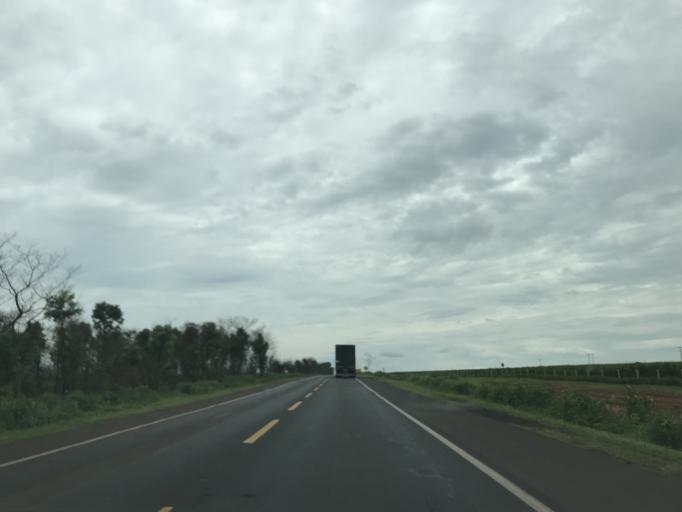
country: BR
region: Minas Gerais
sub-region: Frutal
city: Frutal
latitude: -20.2110
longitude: -49.1379
